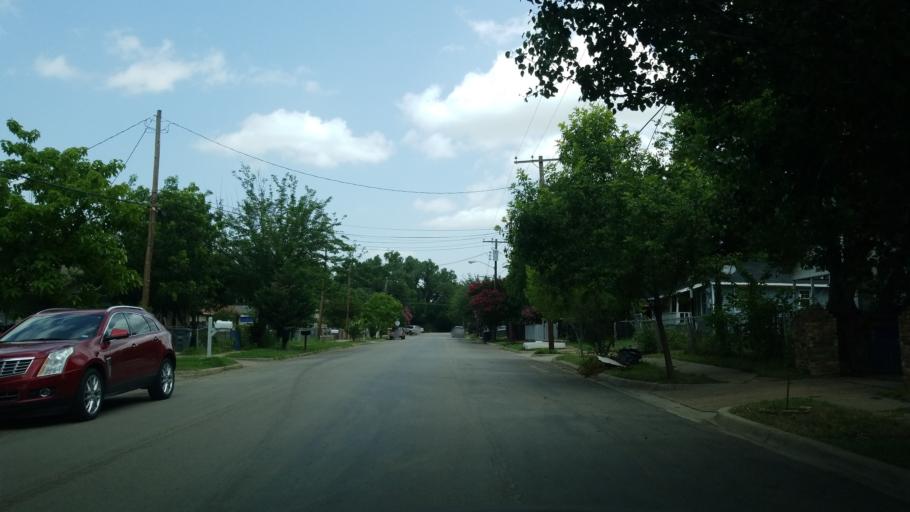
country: US
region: Texas
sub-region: Dallas County
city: Cockrell Hill
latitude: 32.7809
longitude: -96.9094
